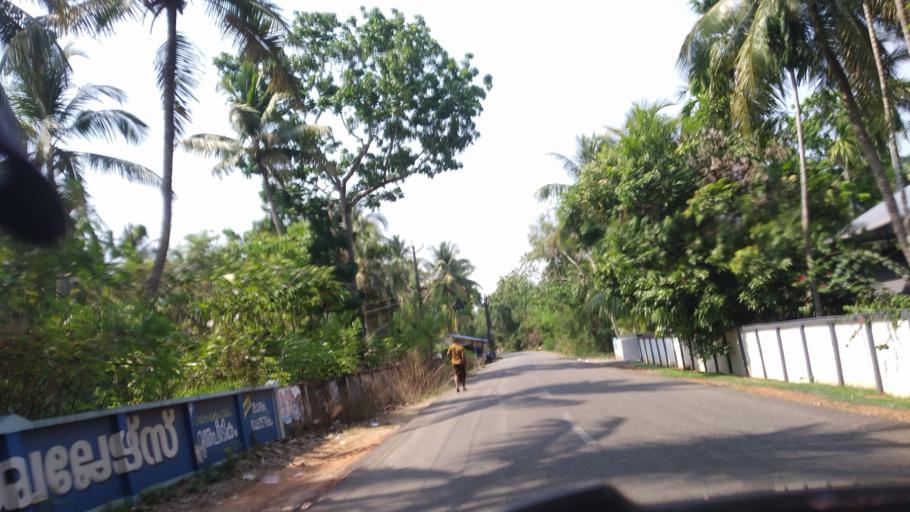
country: IN
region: Kerala
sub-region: Thrissur District
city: Kodungallur
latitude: 10.2892
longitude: 76.1353
